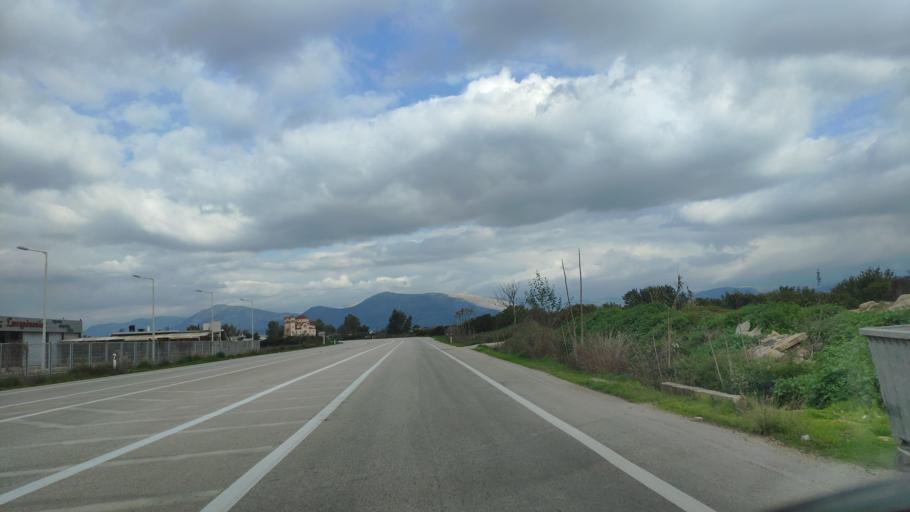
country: GR
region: Peloponnese
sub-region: Nomos Argolidos
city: Argos
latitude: 37.6215
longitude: 22.7355
